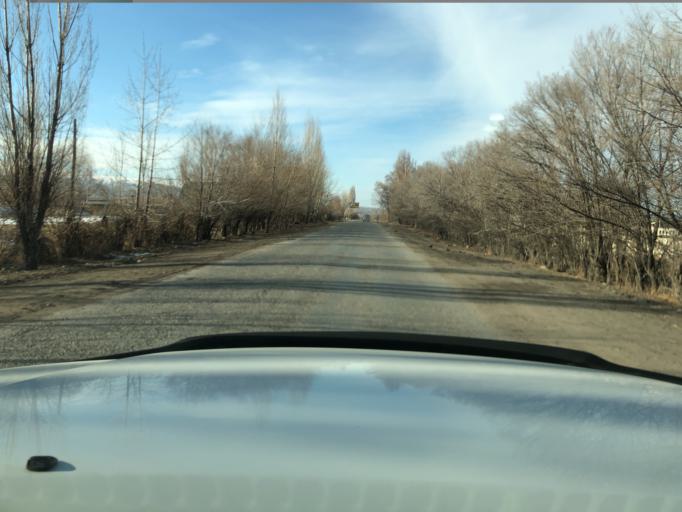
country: KG
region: Ysyk-Koel
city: Pokrovka
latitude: 42.3323
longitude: 77.9790
